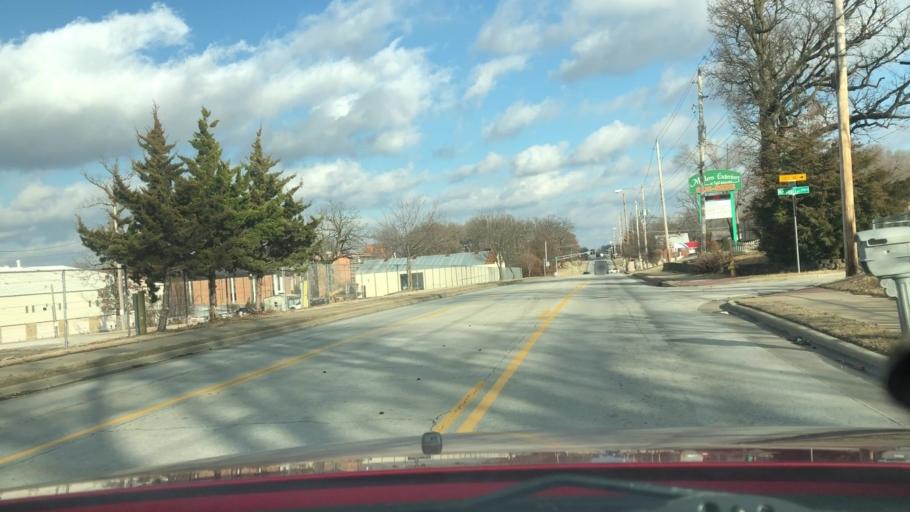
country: US
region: Missouri
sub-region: Greene County
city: Springfield
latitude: 37.2517
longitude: -93.2996
